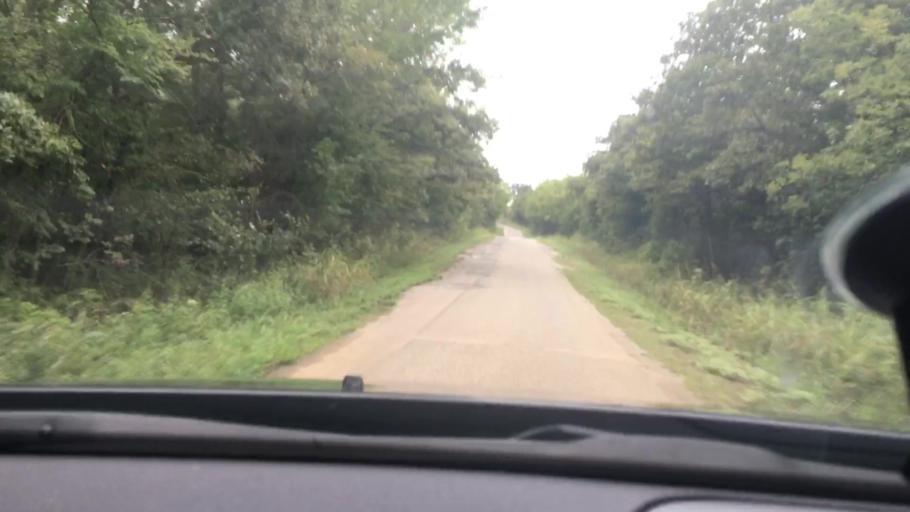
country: US
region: Oklahoma
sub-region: Pontotoc County
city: Byng
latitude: 34.8181
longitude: -96.5350
